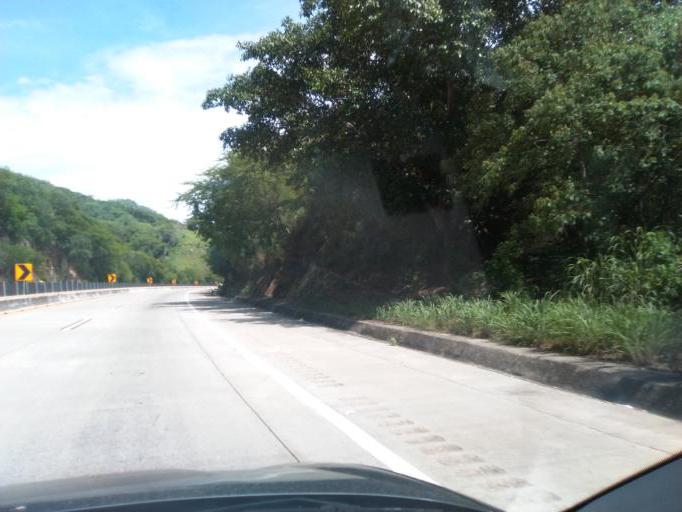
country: MX
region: Guerrero
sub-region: Acapulco de Juarez
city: Pueblo Madero (El Playon)
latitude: 17.0736
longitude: -99.6199
